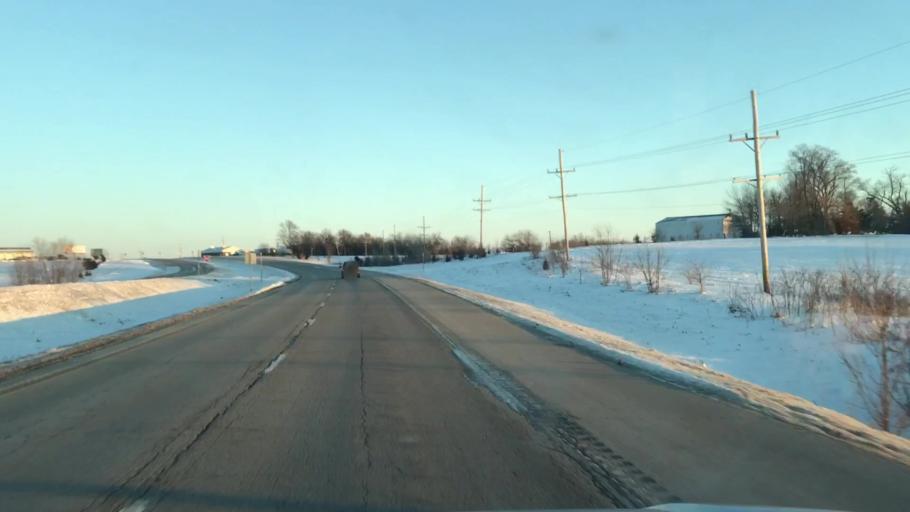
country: US
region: Missouri
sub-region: Clinton County
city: Cameron
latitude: 39.7567
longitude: -94.3433
